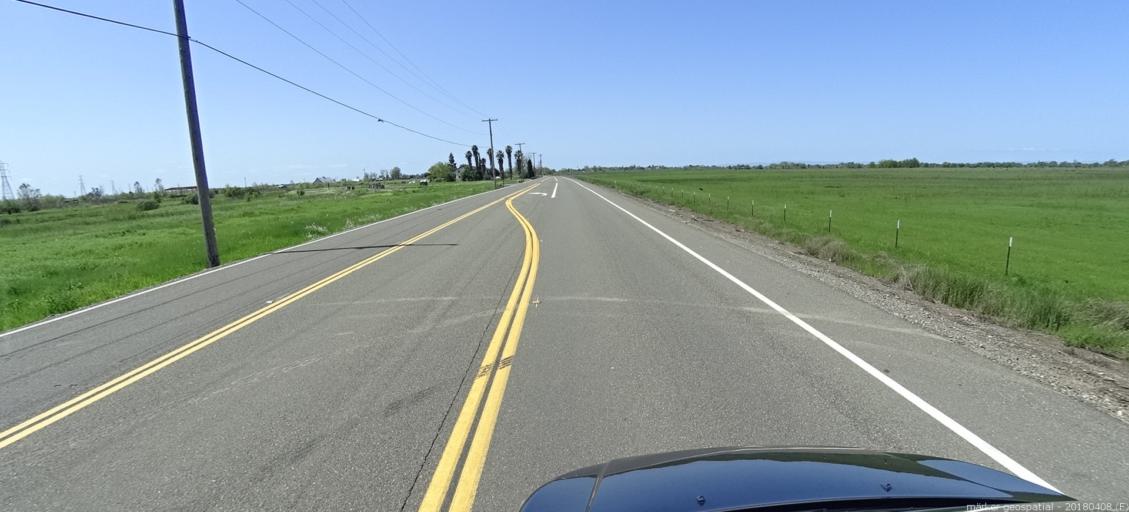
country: US
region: California
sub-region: Sacramento County
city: Laguna
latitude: 38.3722
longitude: -121.4924
